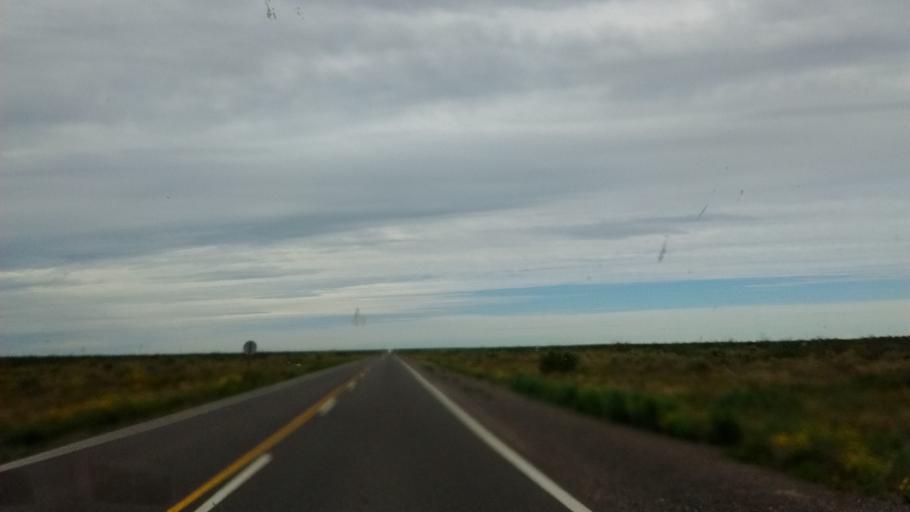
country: AR
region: Rio Negro
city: Catriel
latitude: -38.2594
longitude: -67.9897
